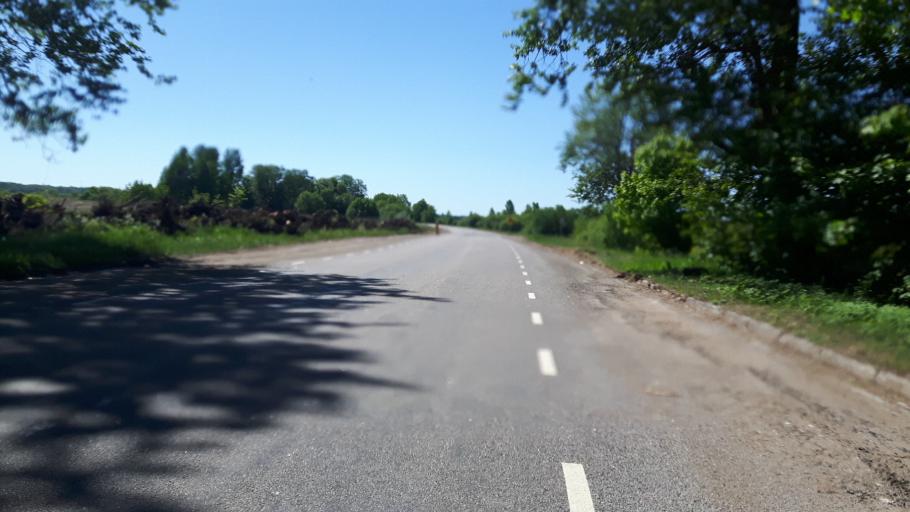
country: EE
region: Ida-Virumaa
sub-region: Narva-Joesuu linn
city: Narva-Joesuu
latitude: 59.3918
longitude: 27.9225
